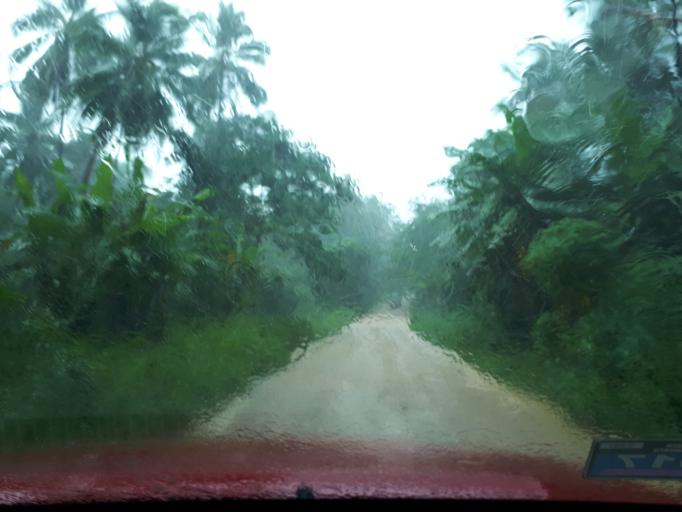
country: VU
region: Sanma
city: Luganville
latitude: -15.5579
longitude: 166.9947
